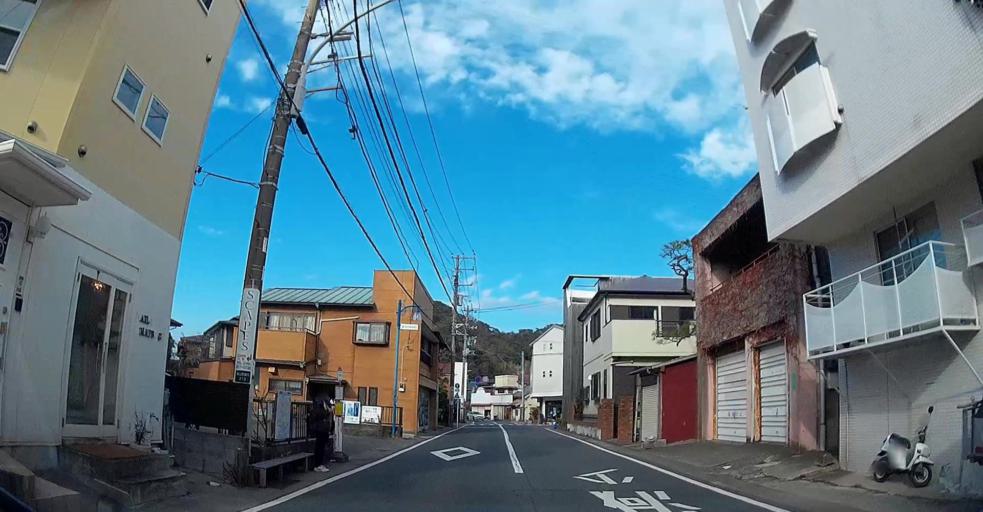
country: JP
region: Kanagawa
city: Hayama
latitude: 35.2772
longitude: 139.5722
